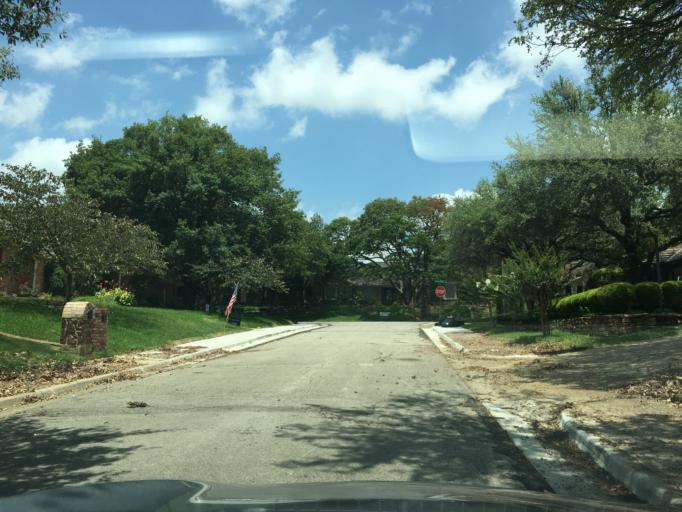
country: US
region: Texas
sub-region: Dallas County
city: Richardson
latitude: 32.9017
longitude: -96.7429
